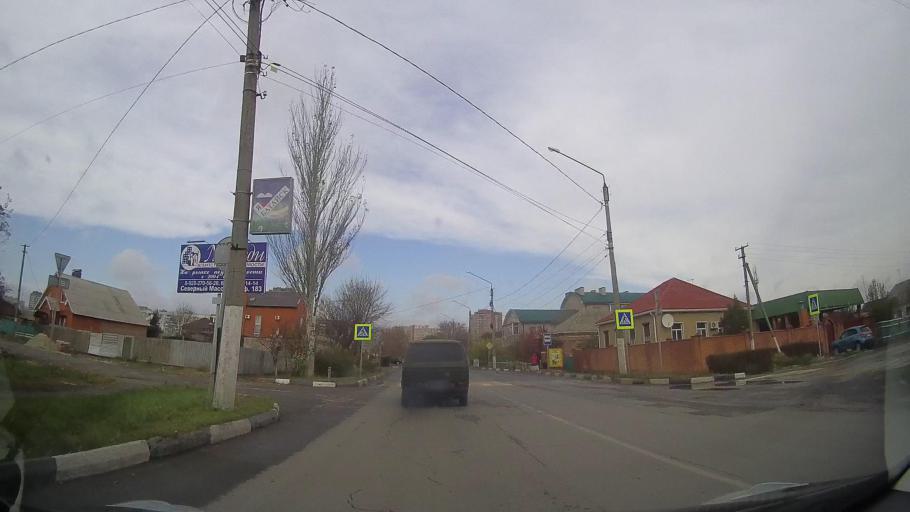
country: RU
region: Rostov
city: Bataysk
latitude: 47.1524
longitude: 39.7472
